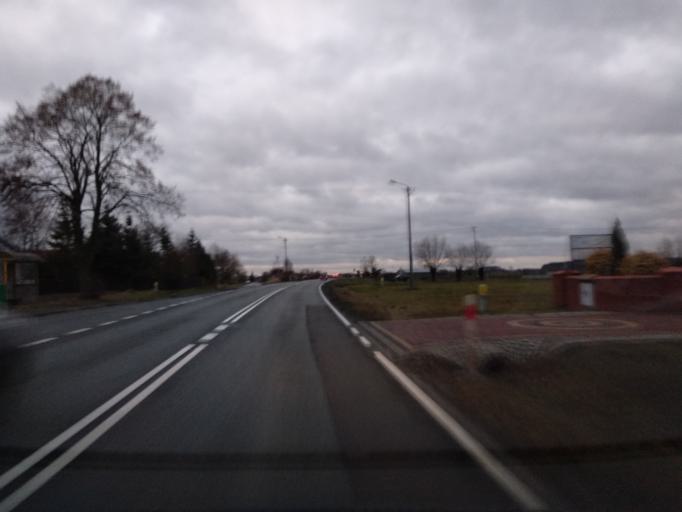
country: PL
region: Greater Poland Voivodeship
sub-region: Powiat koninski
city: Rychwal
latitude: 52.1280
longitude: 18.1778
